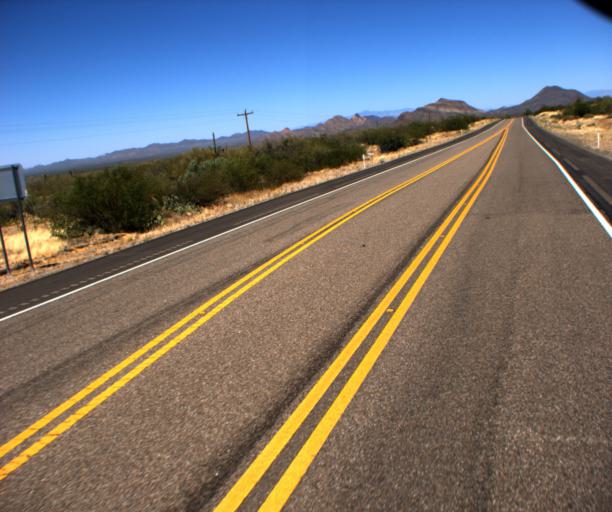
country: US
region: Arizona
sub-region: Pima County
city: Three Points
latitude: 32.0320
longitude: -111.5561
